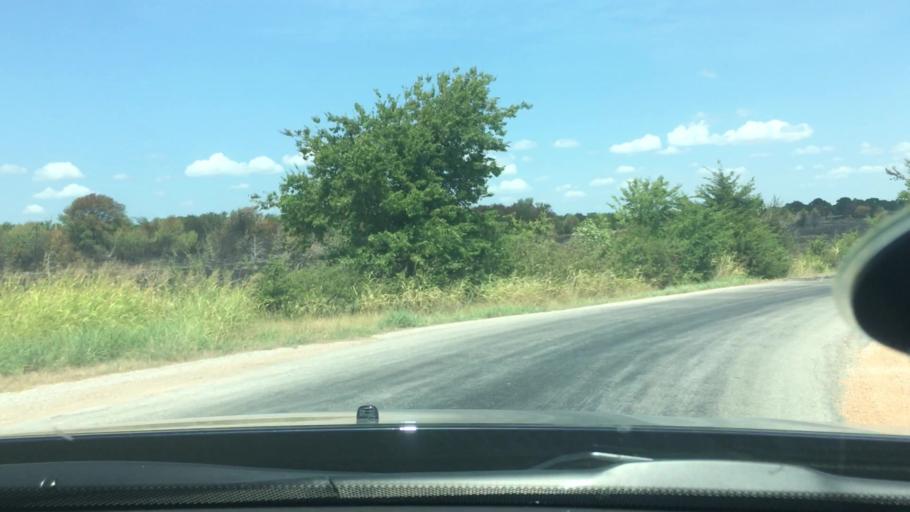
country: US
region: Oklahoma
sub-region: Love County
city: Marietta
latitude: 34.0022
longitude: -97.1934
